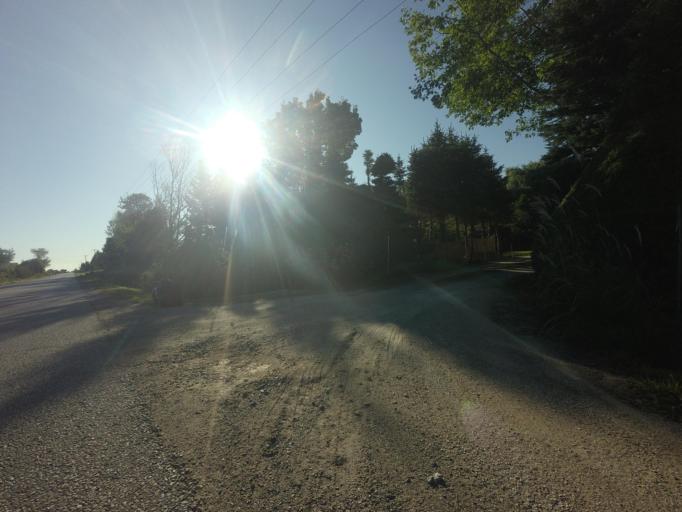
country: CA
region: Ontario
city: Bradford West Gwillimbury
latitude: 44.0532
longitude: -79.7229
